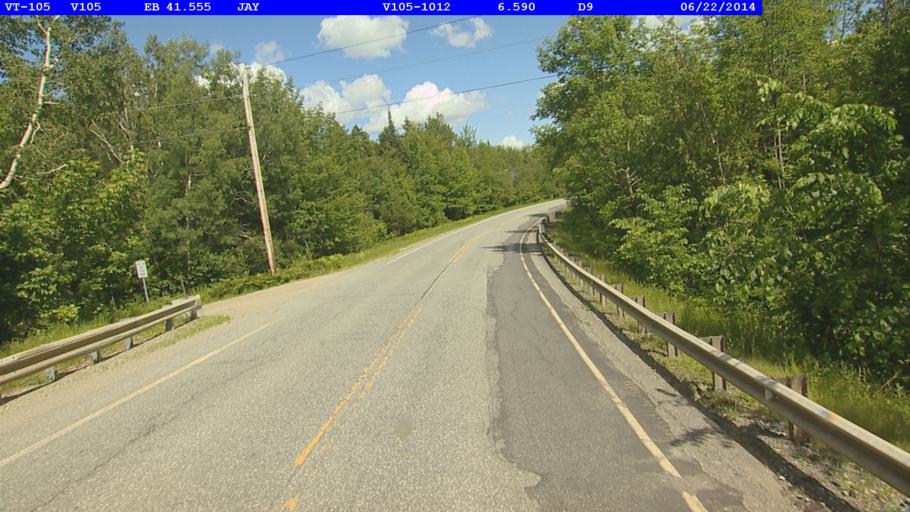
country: CA
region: Quebec
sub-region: Monteregie
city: Sutton
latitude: 44.9725
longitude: -72.4557
